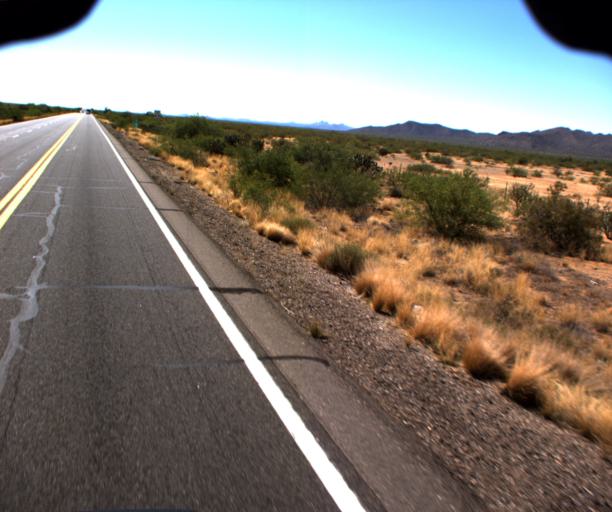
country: US
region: Arizona
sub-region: Yavapai County
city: Congress
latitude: 34.1324
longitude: -112.9635
